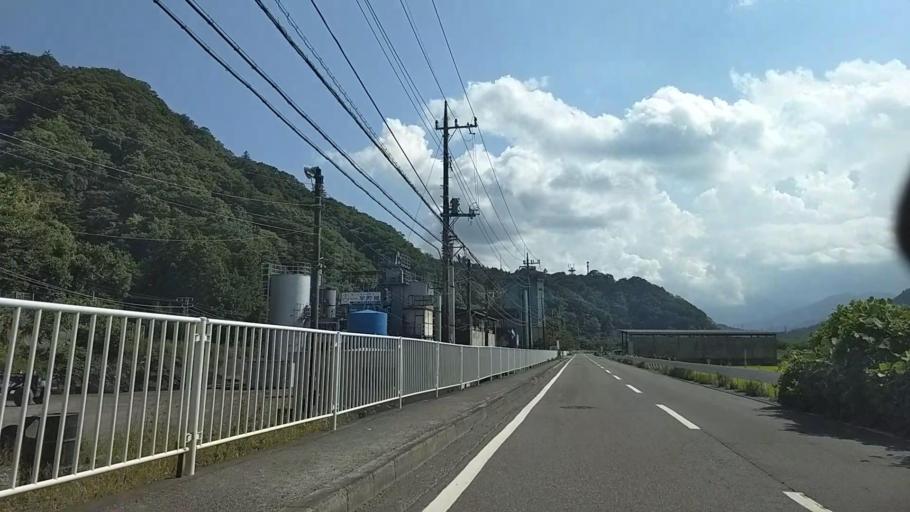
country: JP
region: Shizuoka
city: Fujinomiya
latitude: 35.3842
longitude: 138.4547
